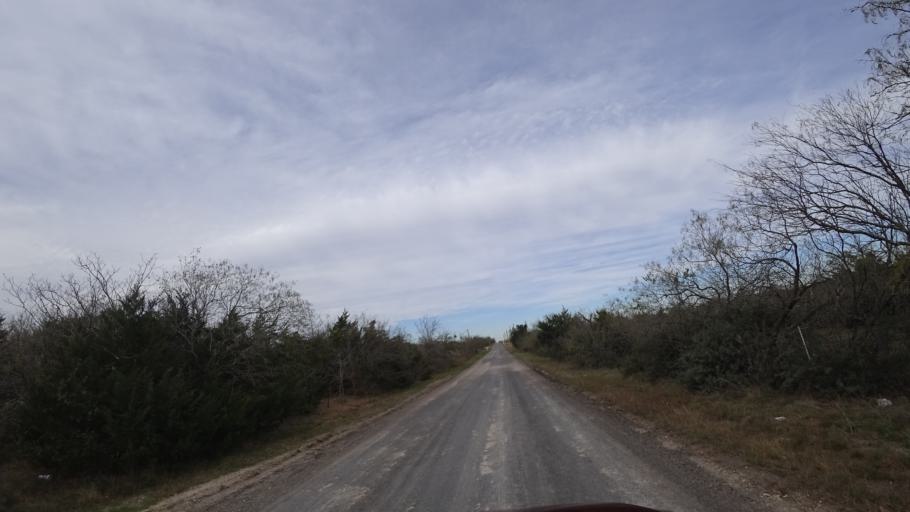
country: US
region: Texas
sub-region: Travis County
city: Garfield
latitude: 30.1104
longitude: -97.5765
